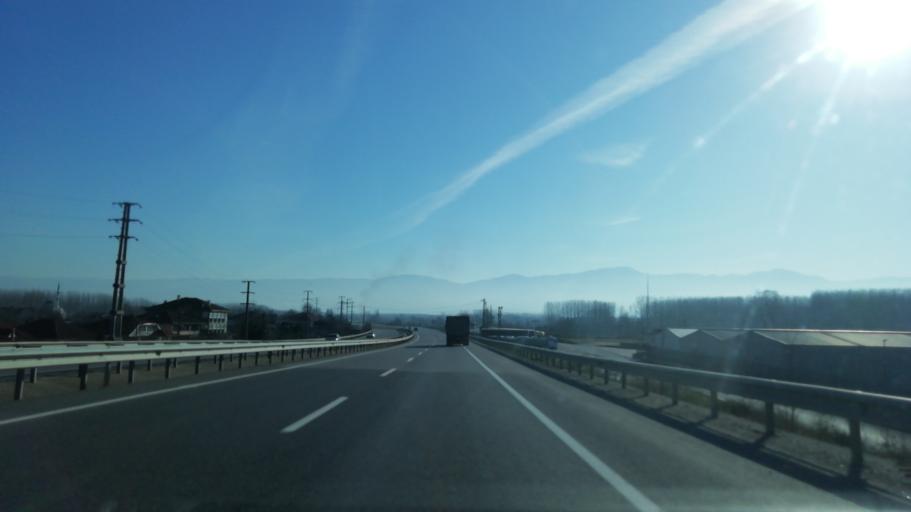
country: TR
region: Sakarya
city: Akyazi
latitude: 40.7159
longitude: 30.5635
